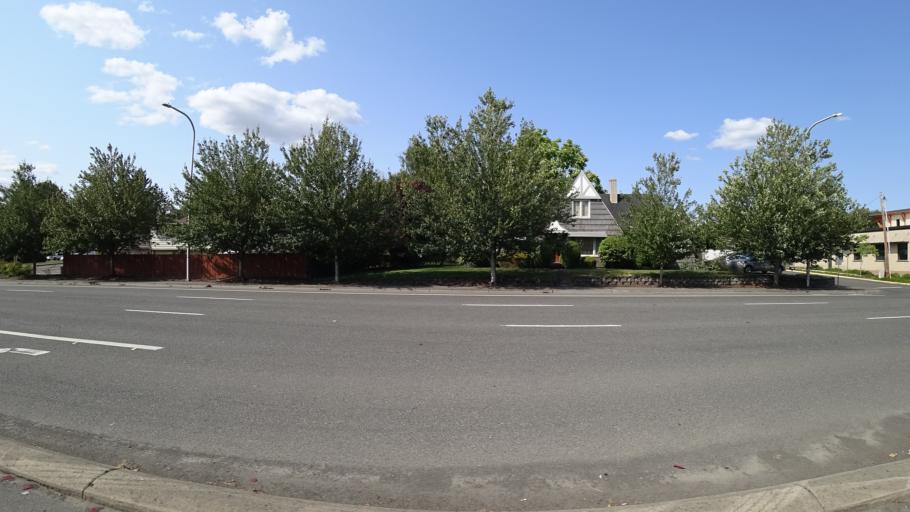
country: US
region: Oregon
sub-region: Clackamas County
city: Sunnyside
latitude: 45.4332
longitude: -122.5481
